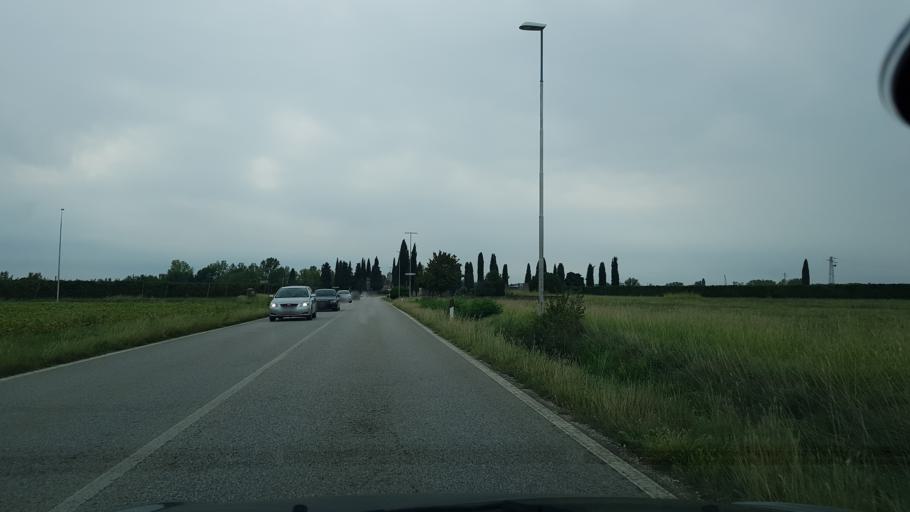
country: IT
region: Friuli Venezia Giulia
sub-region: Provincia di Udine
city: Chiopris
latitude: 45.9354
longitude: 13.3903
